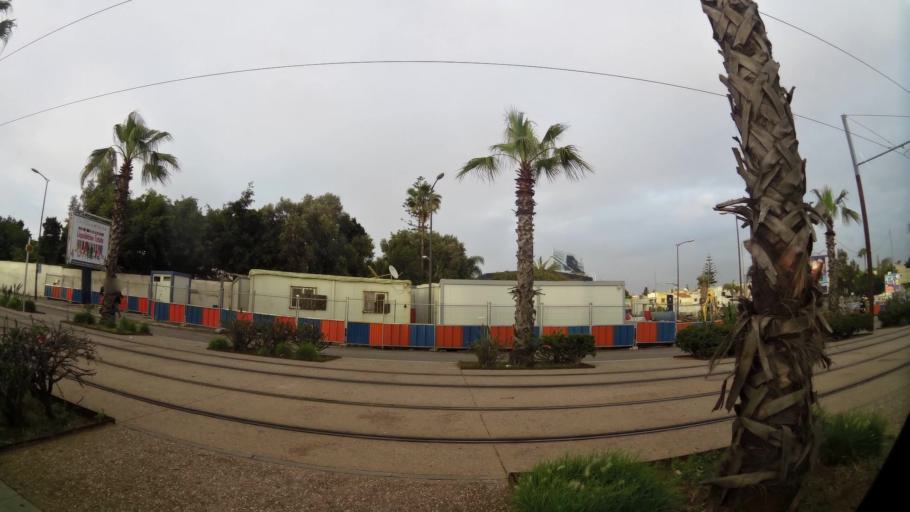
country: MA
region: Grand Casablanca
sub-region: Casablanca
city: Casablanca
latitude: 33.5776
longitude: -7.6737
